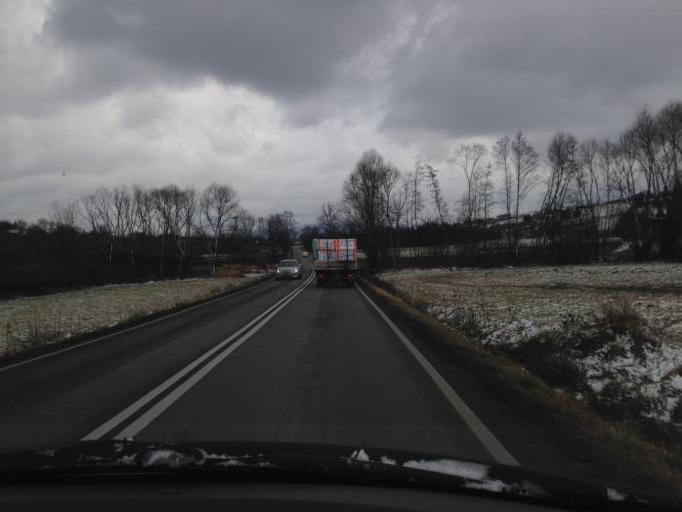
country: PL
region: Lesser Poland Voivodeship
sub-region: Powiat bochenski
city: Lapanow
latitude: 49.8613
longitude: 20.3297
